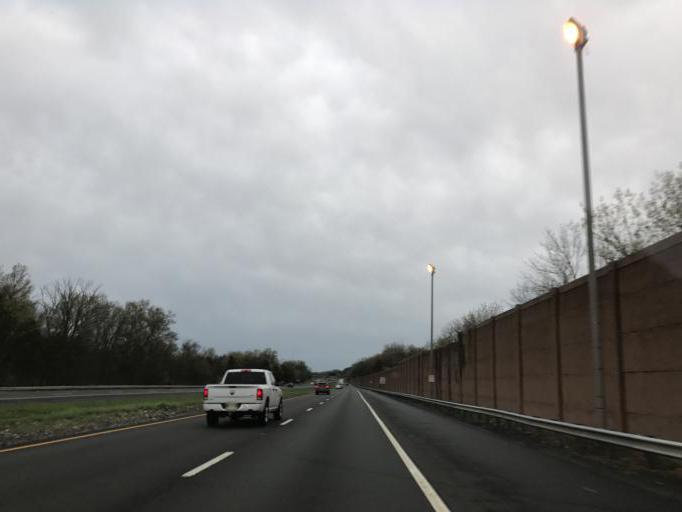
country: US
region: New Jersey
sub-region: Somerset County
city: Bridgewater
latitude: 40.6320
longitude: -74.6443
